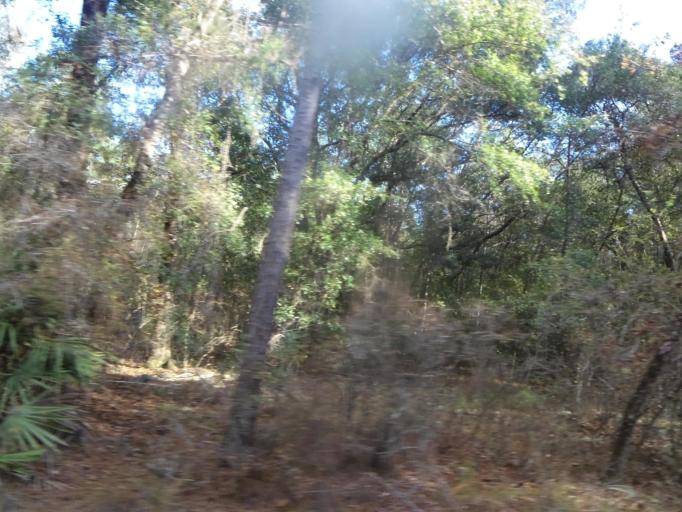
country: US
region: Florida
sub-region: Clay County
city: Middleburg
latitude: 30.1331
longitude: -81.9415
